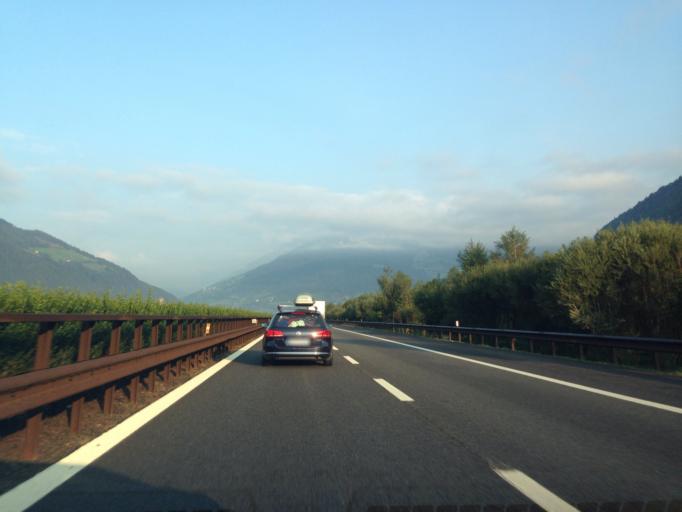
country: IT
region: Trentino-Alto Adige
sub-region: Bolzano
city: Campo di Trens
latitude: 46.8727
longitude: 11.4706
